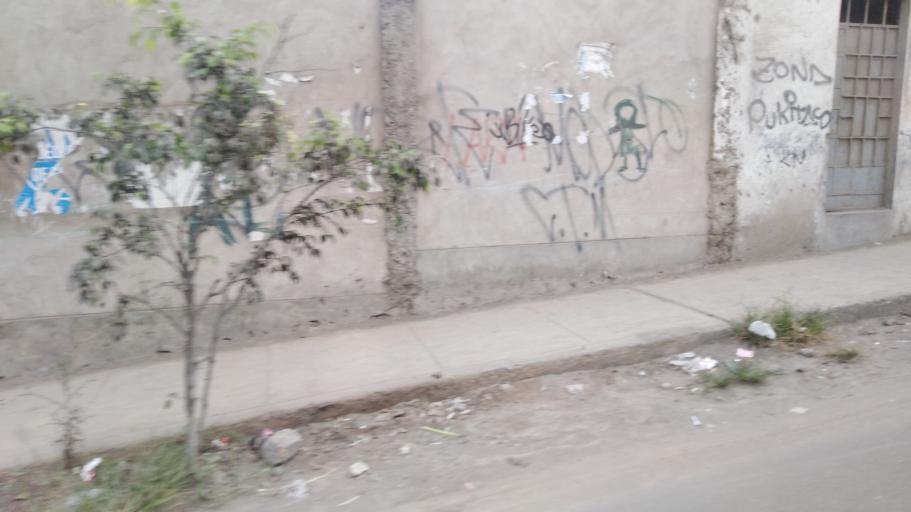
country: PE
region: Lima
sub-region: Lima
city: La Molina
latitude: -12.1426
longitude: -76.9419
